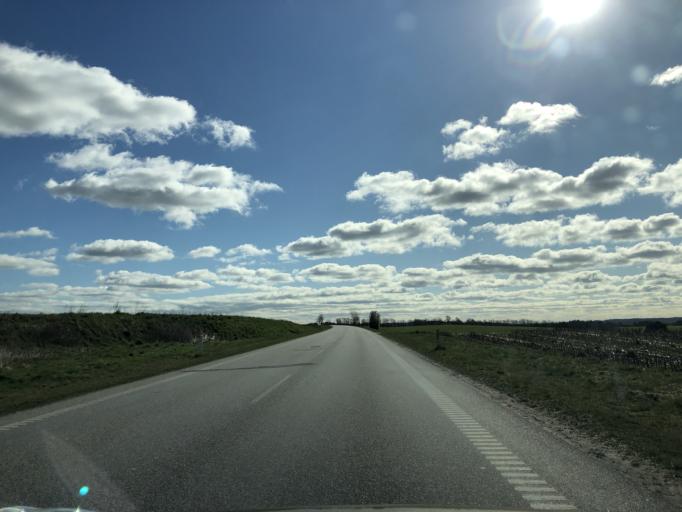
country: DK
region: North Denmark
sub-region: Vesthimmerland Kommune
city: Alestrup
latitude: 56.6154
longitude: 9.6172
